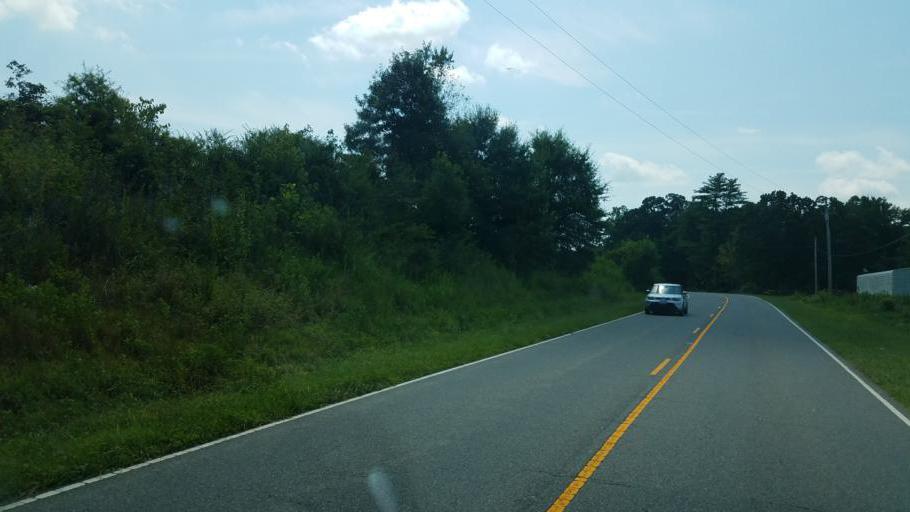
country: US
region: North Carolina
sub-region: Gaston County
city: Cherryville
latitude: 35.4164
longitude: -81.4087
